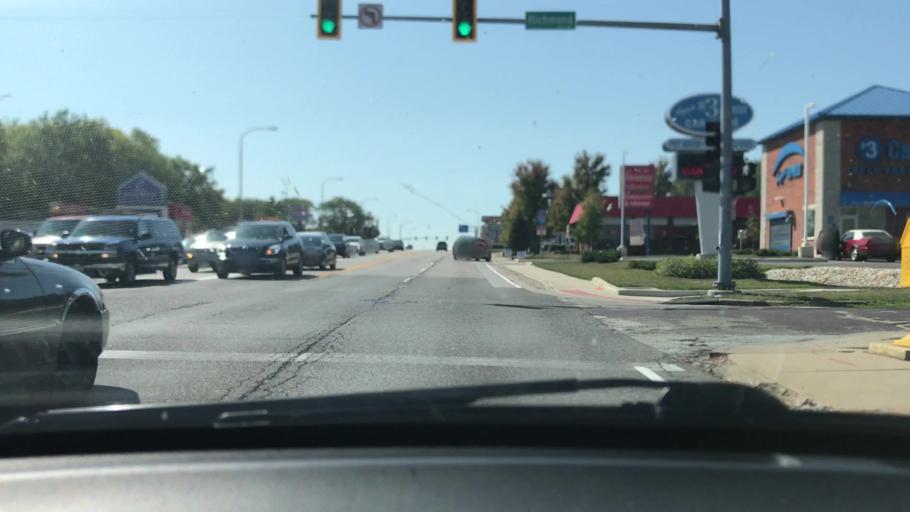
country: US
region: Illinois
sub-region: Peoria County
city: North Peoria
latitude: 40.7080
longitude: -89.5941
